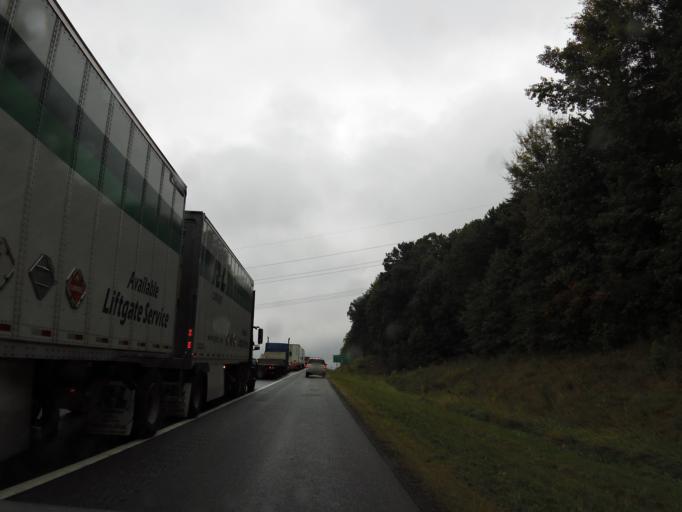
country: US
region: Tennessee
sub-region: Bradley County
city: Hopewell
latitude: 35.2188
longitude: -84.8625
